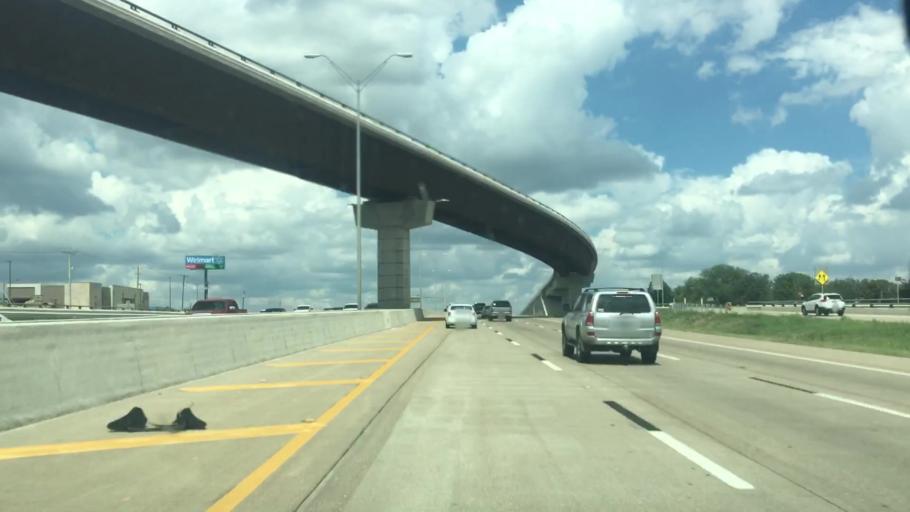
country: US
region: Texas
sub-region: McLennan County
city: Hewitt
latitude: 31.4588
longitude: -97.1719
